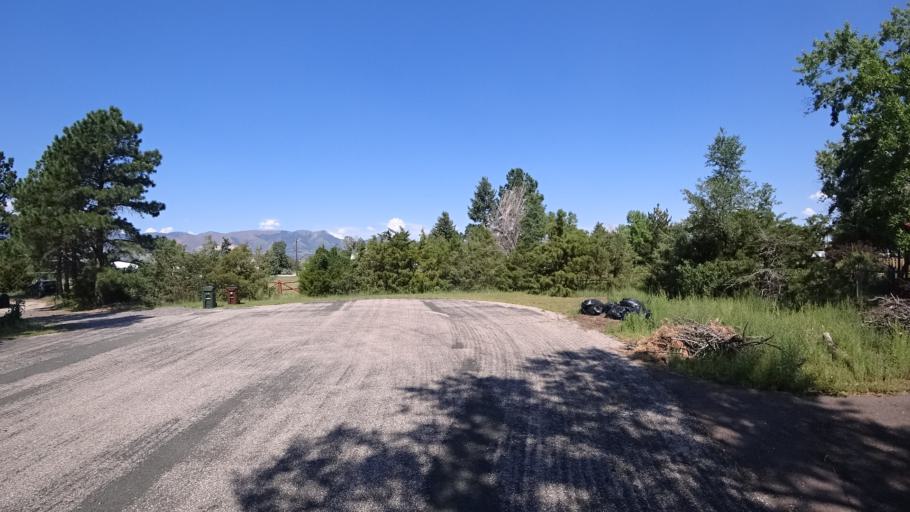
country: US
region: Colorado
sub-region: El Paso County
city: Air Force Academy
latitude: 38.9339
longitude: -104.7882
